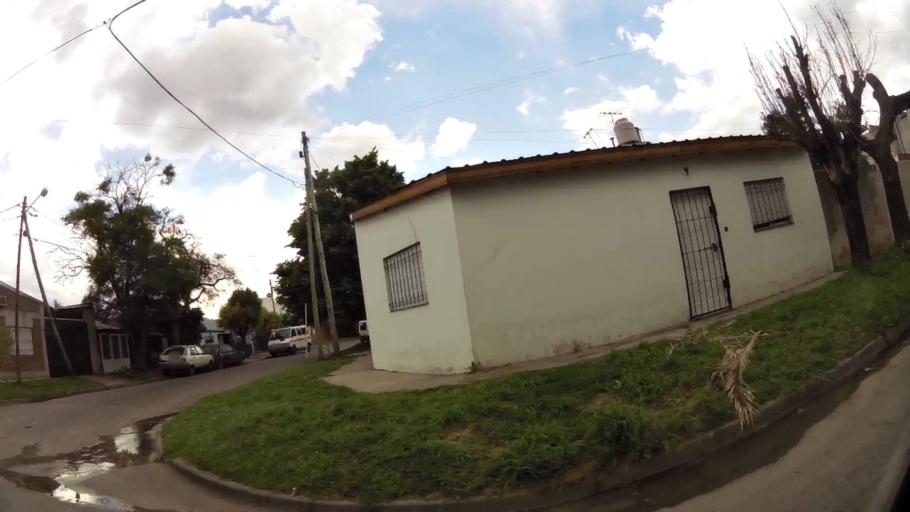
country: AR
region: Buenos Aires
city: Ituzaingo
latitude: -34.6419
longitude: -58.6789
